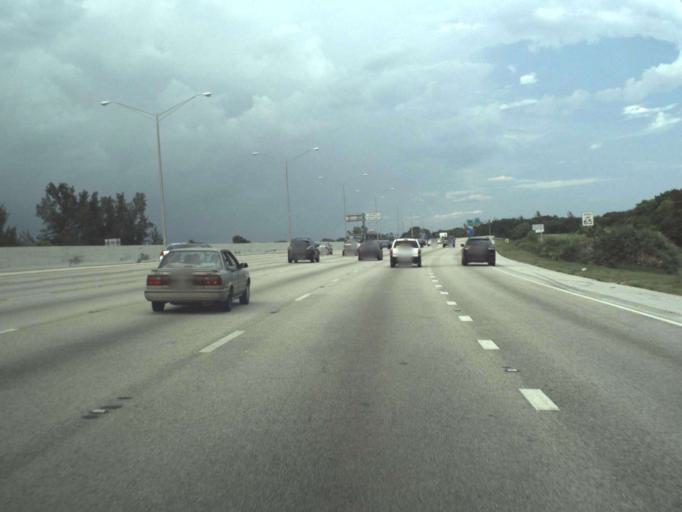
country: US
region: Florida
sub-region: Palm Beach County
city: Lake Clarke Shores
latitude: 26.6427
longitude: -80.0688
